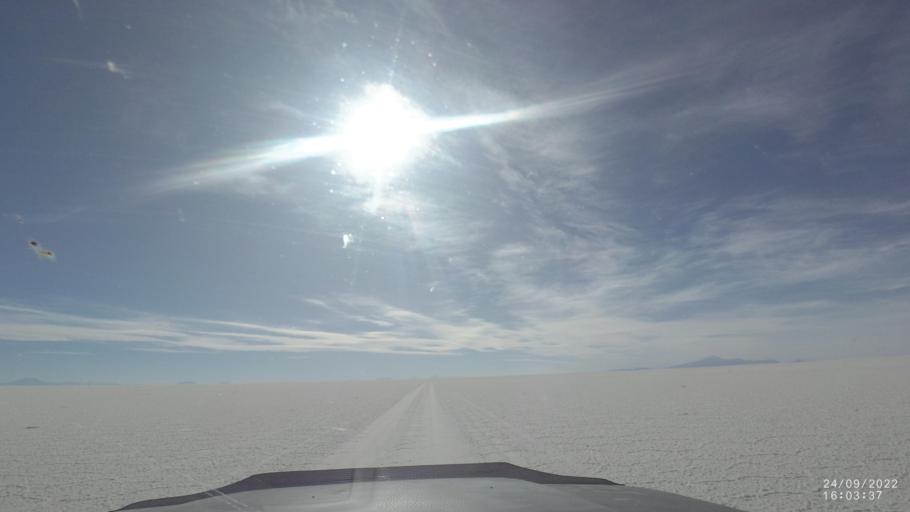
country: BO
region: Potosi
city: Colchani
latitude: -20.3128
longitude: -67.2841
